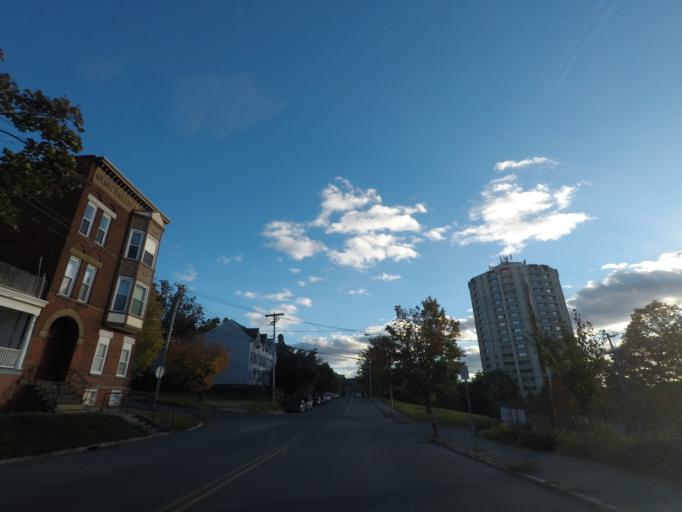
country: US
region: New York
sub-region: Rensselaer County
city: Troy
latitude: 42.7355
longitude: -73.6829
